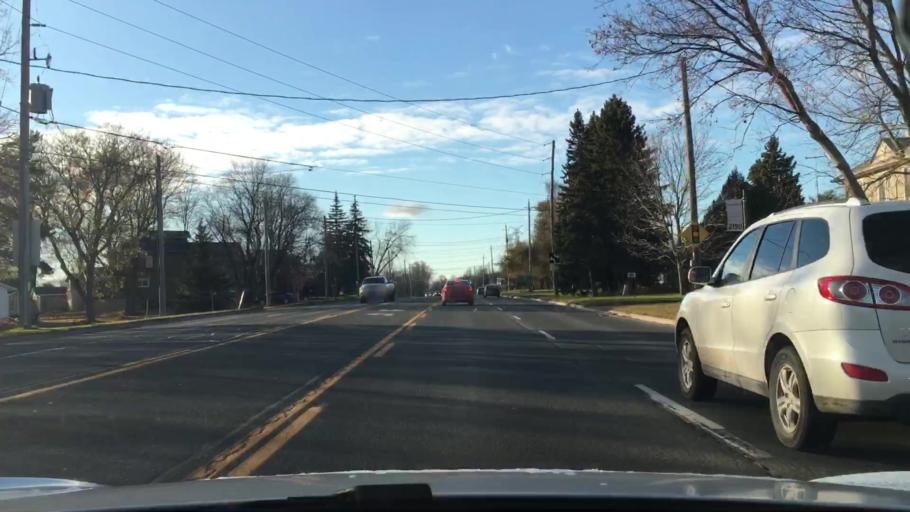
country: CA
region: Ontario
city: Oshawa
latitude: 43.9119
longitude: -78.7308
